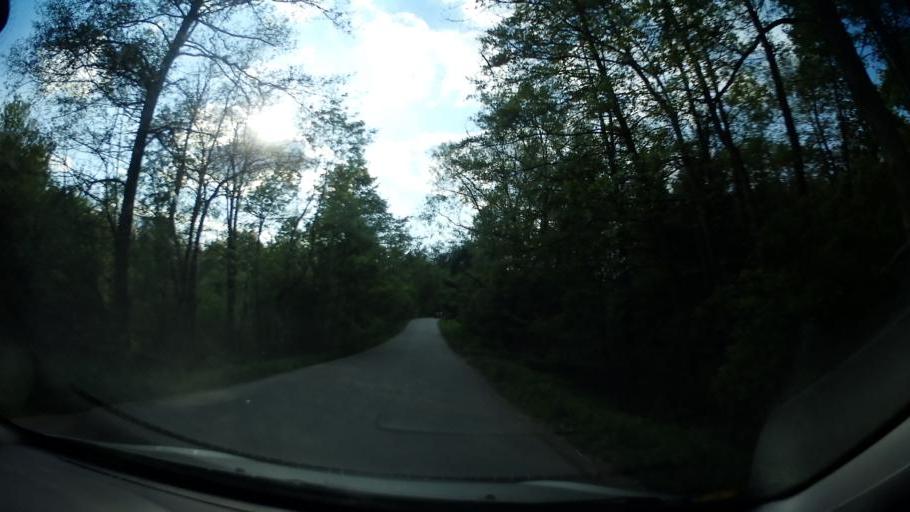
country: CZ
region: Vysocina
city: Budisov
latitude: 49.2816
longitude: 15.9983
